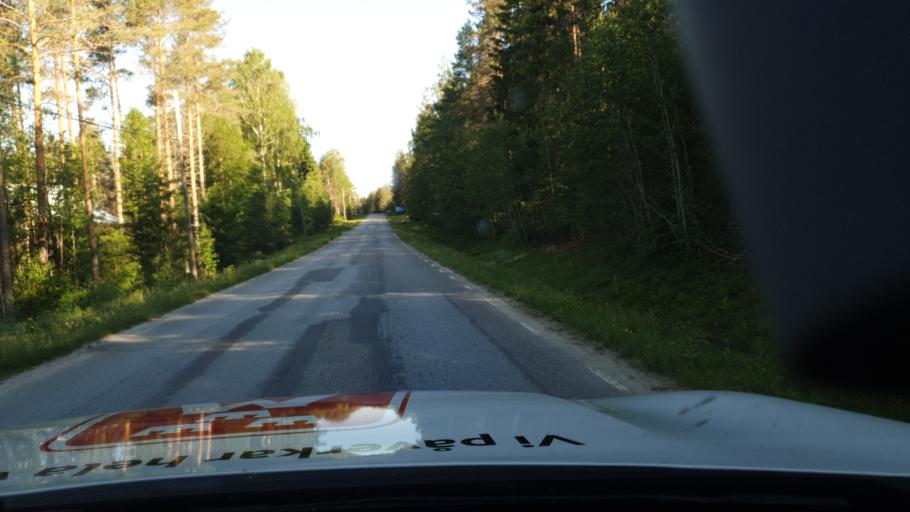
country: SE
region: Vaesterbotten
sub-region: Vannas Kommun
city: Vannasby
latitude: 64.0775
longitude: 20.0571
